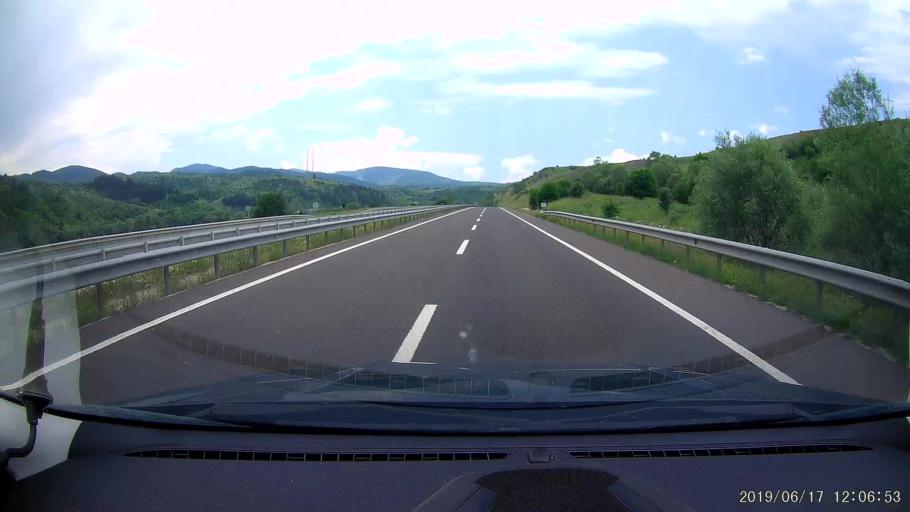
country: TR
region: Cankiri
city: Cerkes
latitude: 40.8373
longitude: 32.7468
